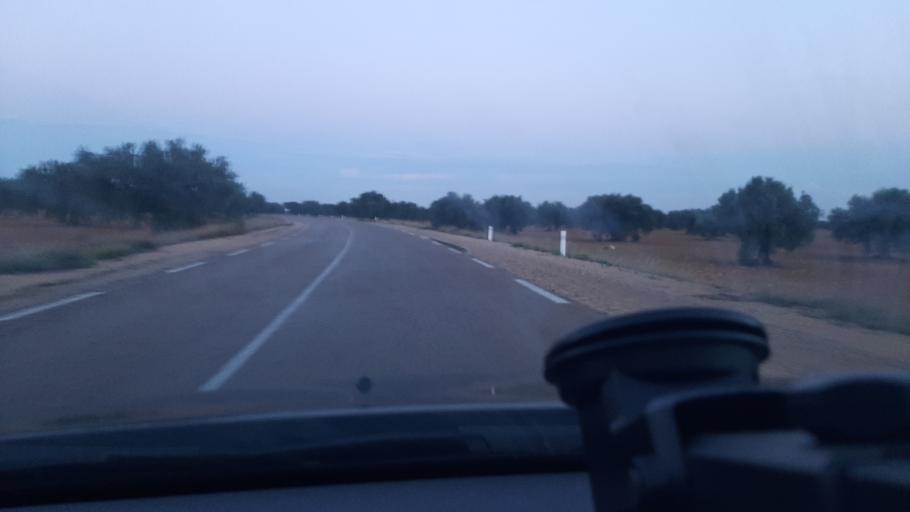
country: TN
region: Al Mahdiyah
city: Shurban
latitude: 35.0343
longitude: 10.5179
